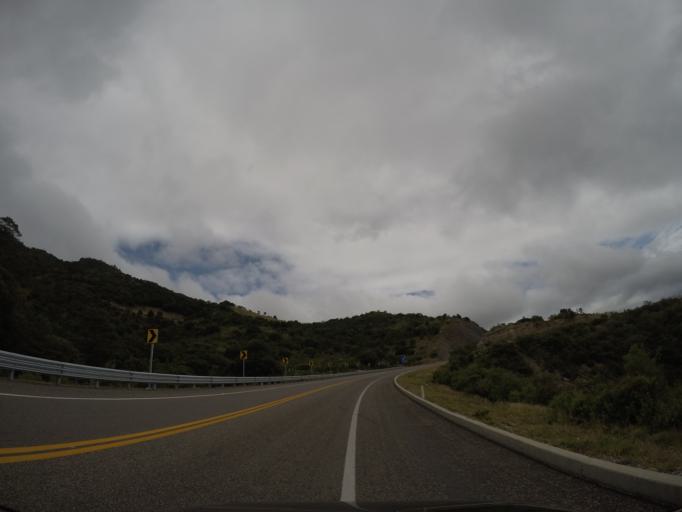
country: MX
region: Oaxaca
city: San Lorenzo Albarradas
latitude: 16.9310
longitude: -96.2669
